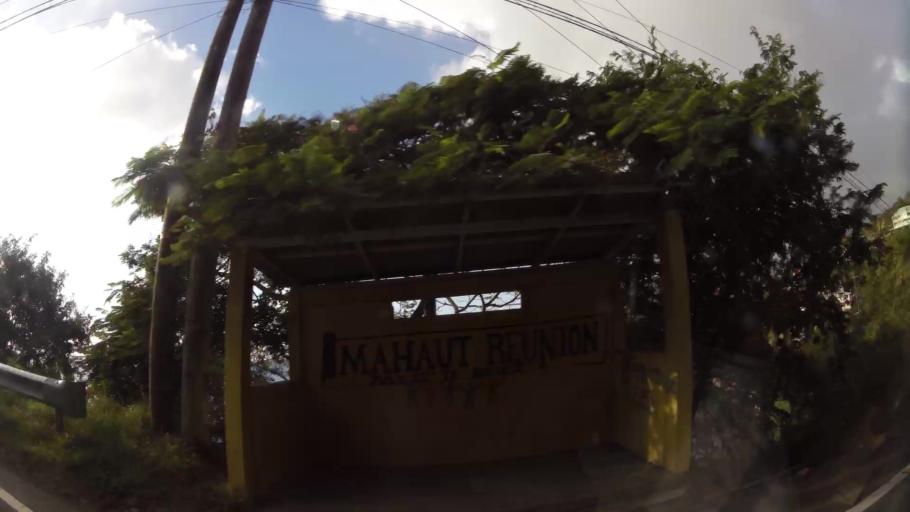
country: DM
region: Saint Paul
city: Mahaut
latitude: 15.3579
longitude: -61.3955
